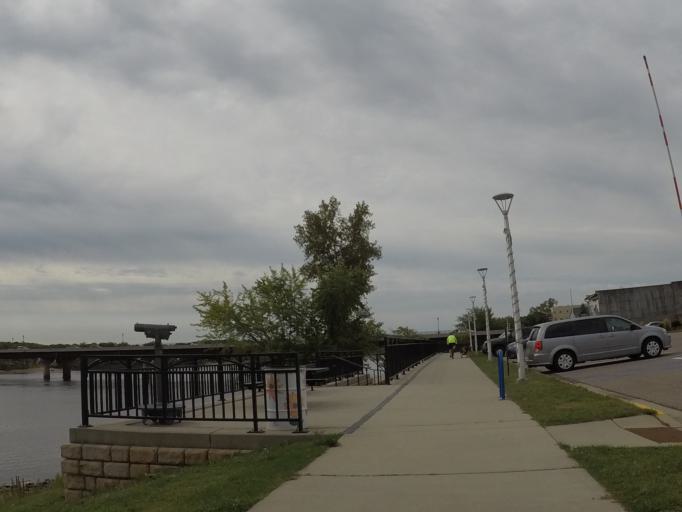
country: US
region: Wisconsin
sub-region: Sauk County
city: Sauk City
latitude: 43.2720
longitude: -89.7205
